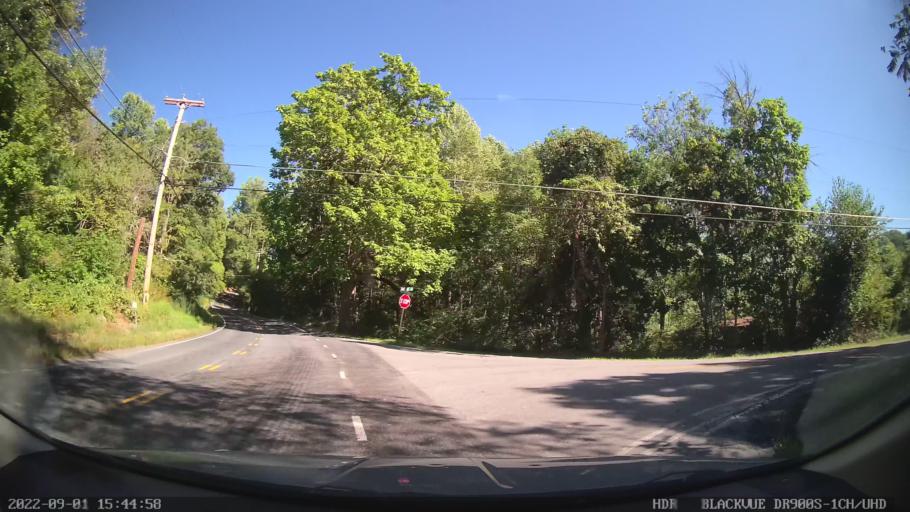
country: US
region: Pennsylvania
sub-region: Berks County
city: Topton
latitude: 40.4704
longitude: -75.6940
